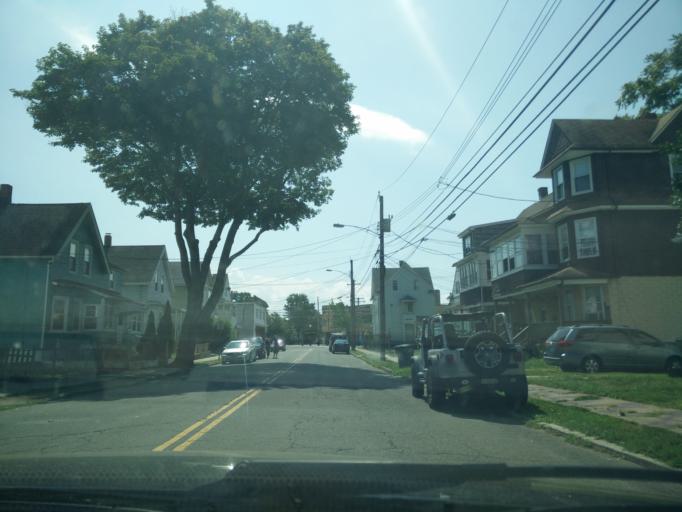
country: US
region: Connecticut
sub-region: Fairfield County
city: Bridgeport
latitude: 41.1567
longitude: -73.2299
